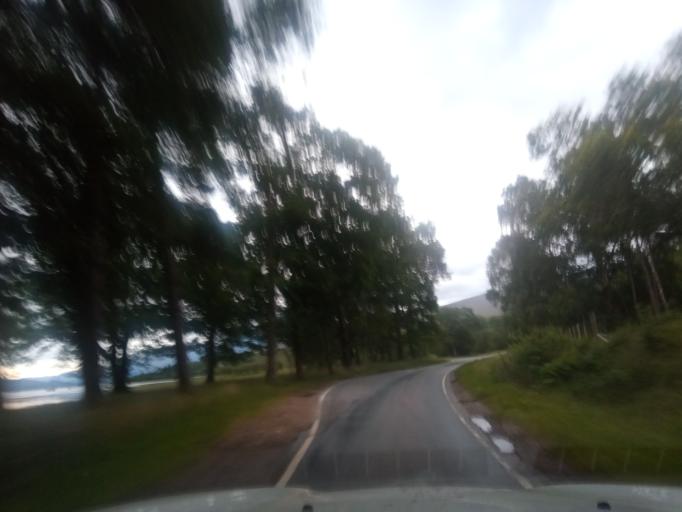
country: GB
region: Scotland
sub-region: Highland
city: Fort William
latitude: 56.8484
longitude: -5.3175
